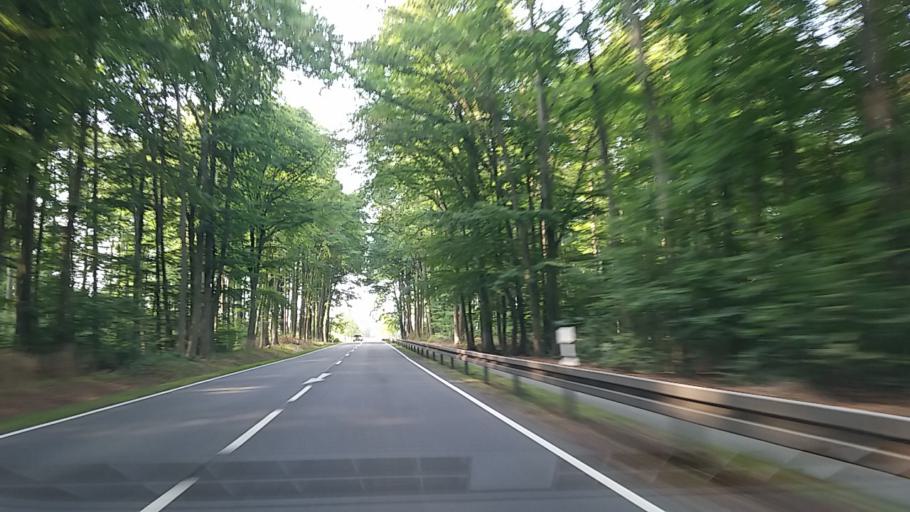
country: DE
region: Mecklenburg-Vorpommern
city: Hagenow
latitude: 53.4111
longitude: 11.1275
